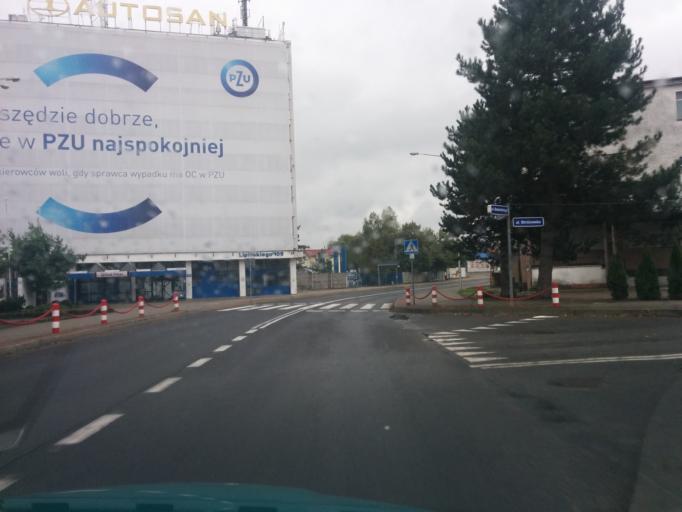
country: PL
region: Subcarpathian Voivodeship
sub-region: Powiat sanocki
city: Sanok
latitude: 49.5478
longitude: 22.2169
